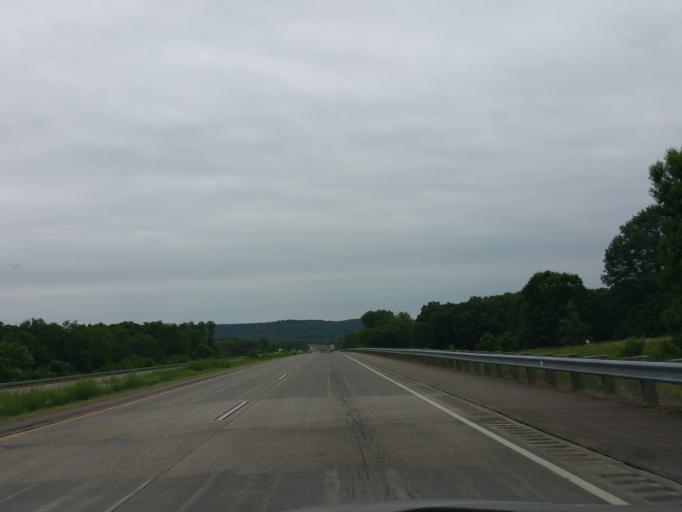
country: US
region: Wisconsin
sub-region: Eau Claire County
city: Eau Claire
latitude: 44.7972
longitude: -91.5525
